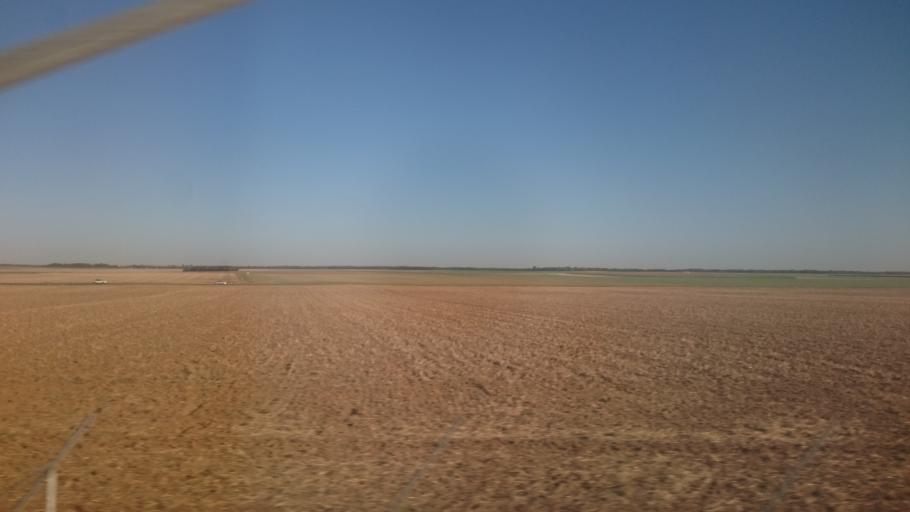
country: FR
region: Centre
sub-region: Departement d'Eure-et-Loir
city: Bonneval
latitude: 48.2245
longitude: 1.4571
